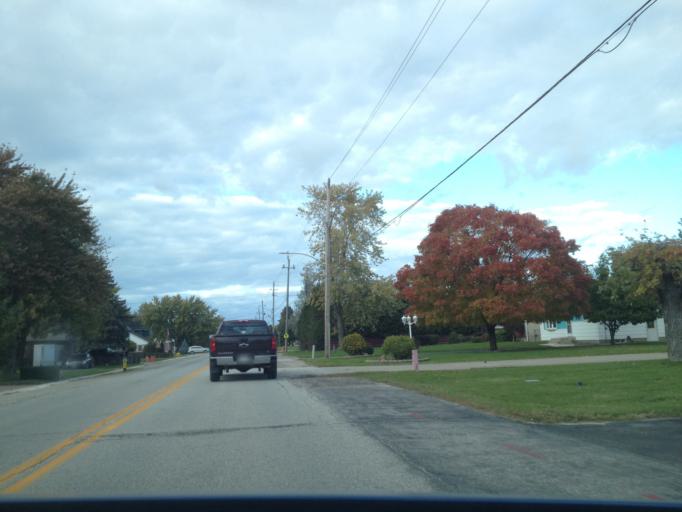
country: US
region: Michigan
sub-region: Wayne County
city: Grosse Pointe Farms
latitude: 42.2864
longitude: -82.7122
